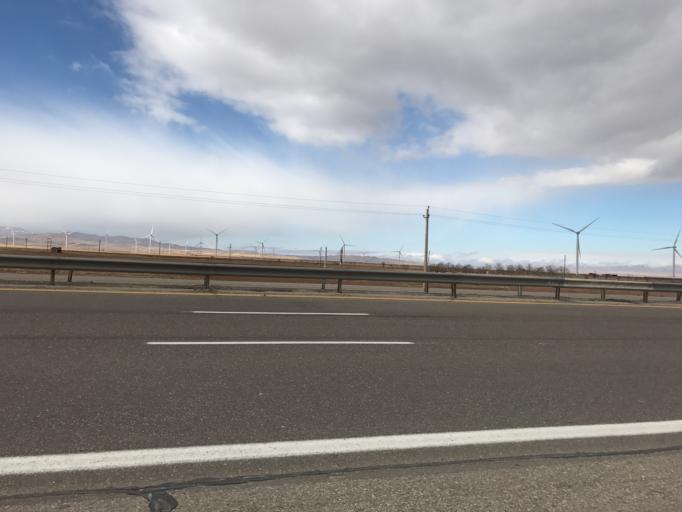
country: IR
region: Qazvin
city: Takestan
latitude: 36.1156
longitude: 49.7418
